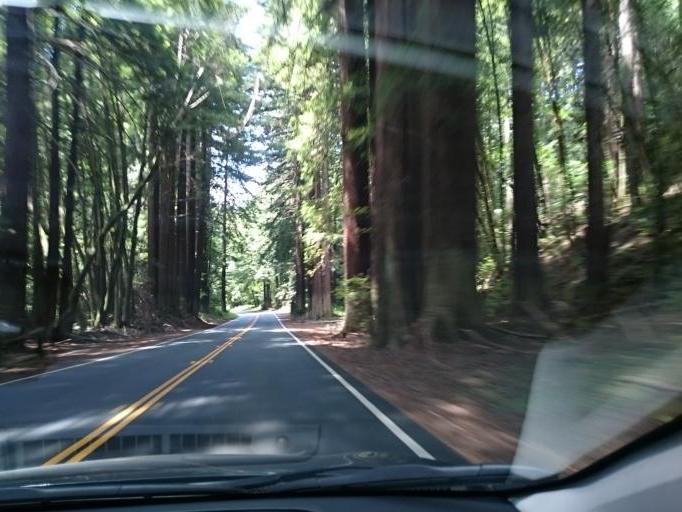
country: US
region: California
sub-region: Mendocino County
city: Fort Bragg
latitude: 39.1678
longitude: -123.6599
